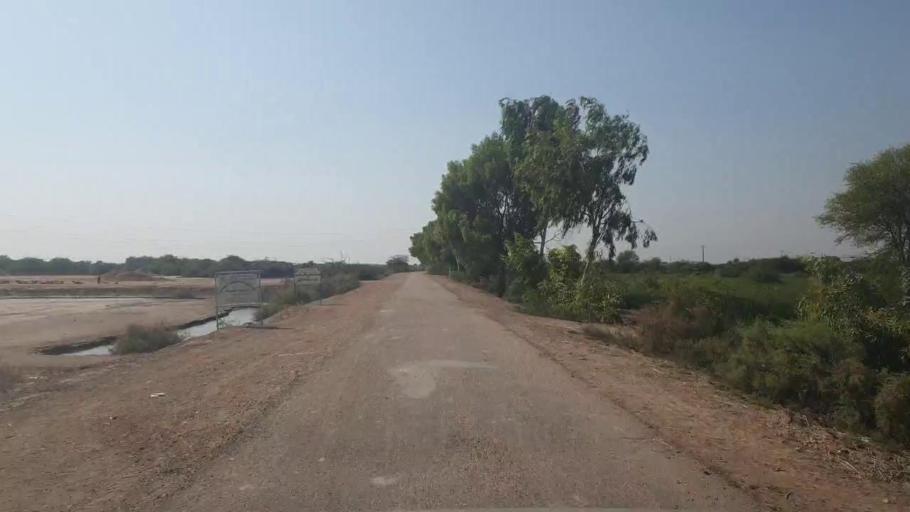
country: PK
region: Sindh
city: Badin
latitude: 24.5544
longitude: 68.8338
